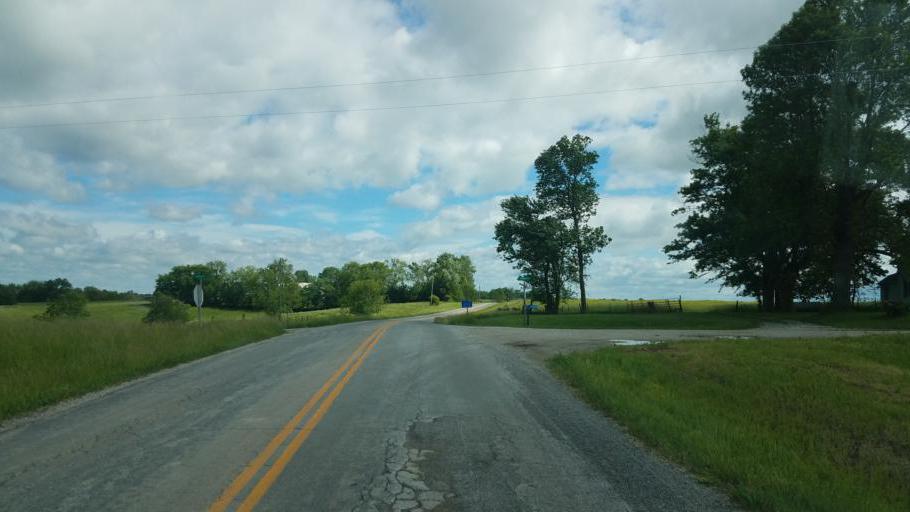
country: US
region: Missouri
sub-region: Mercer County
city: Princeton
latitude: 40.2936
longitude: -93.6806
